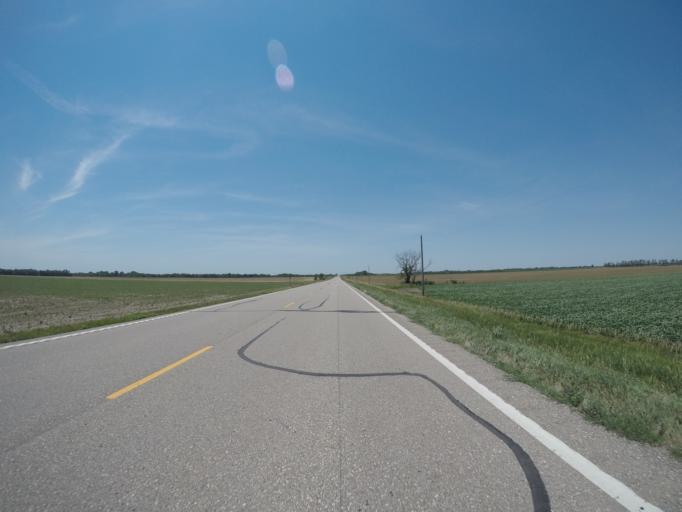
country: US
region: Kansas
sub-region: Dickinson County
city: Solomon
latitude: 39.0307
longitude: -97.4742
